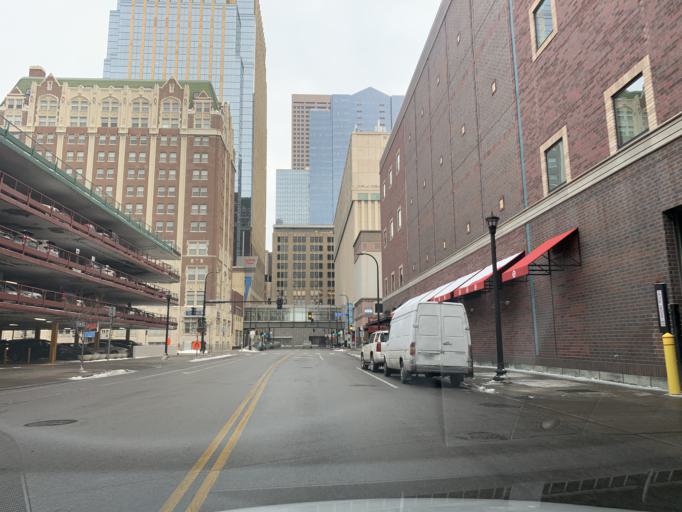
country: US
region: Minnesota
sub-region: Hennepin County
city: Minneapolis
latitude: 44.9749
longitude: -93.2758
